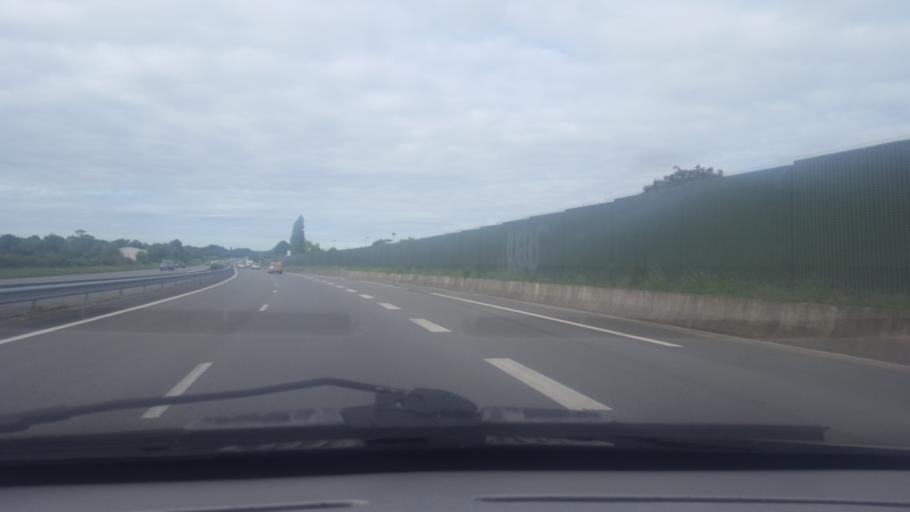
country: FR
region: Pays de la Loire
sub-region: Departement de la Loire-Atlantique
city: Saint-Philbert-de-Grand-Lieu
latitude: 47.0357
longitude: -1.6545
